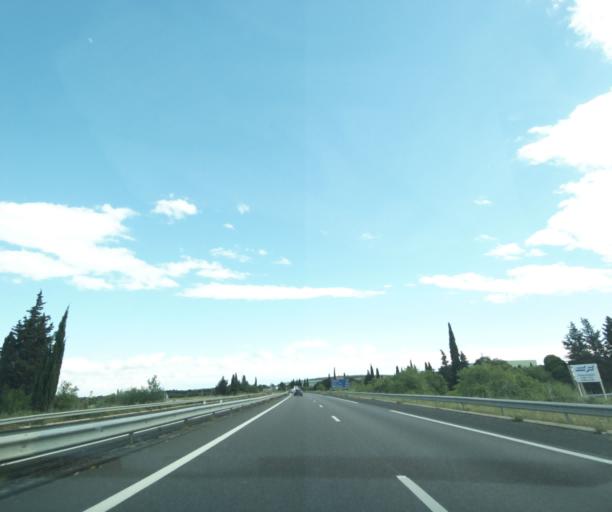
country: FR
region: Languedoc-Roussillon
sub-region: Departement du Gard
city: Garons
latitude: 43.7526
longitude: 4.4308
